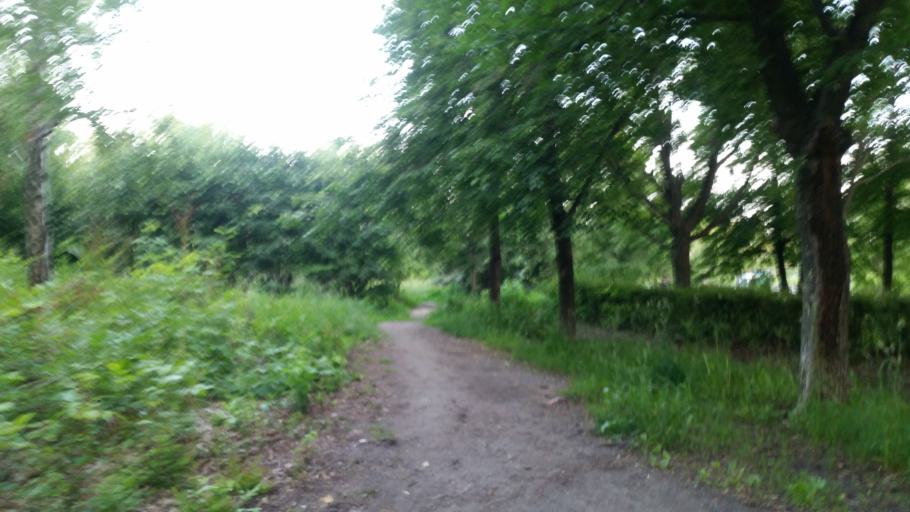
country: RU
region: Ulyanovsk
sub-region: Ulyanovskiy Rayon
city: Ulyanovsk
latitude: 54.3438
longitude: 48.3983
